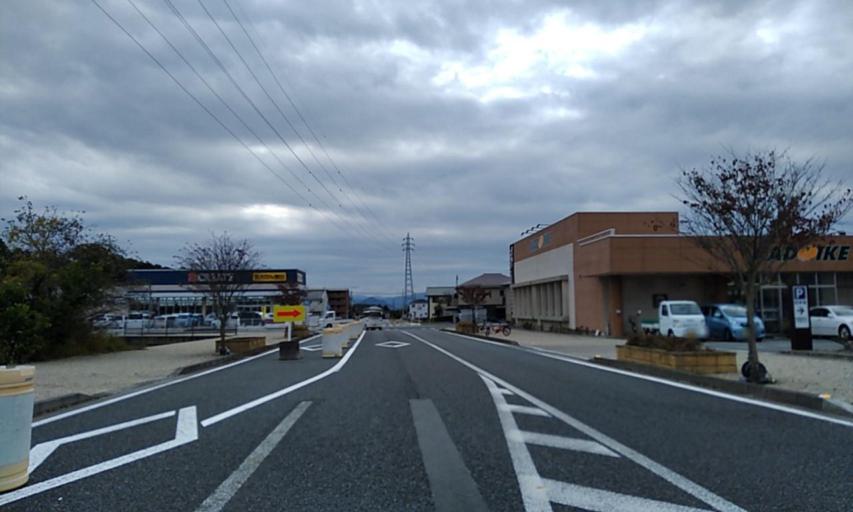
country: JP
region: Shizuoka
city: Mishima
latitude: 35.1741
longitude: 138.9158
